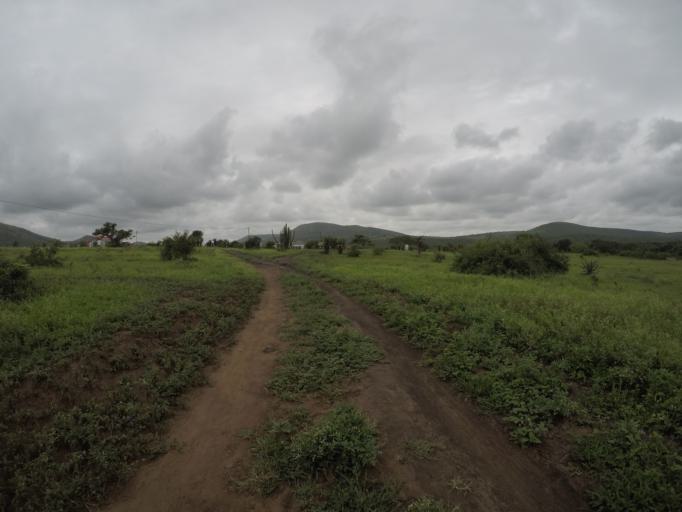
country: ZA
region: KwaZulu-Natal
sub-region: uThungulu District Municipality
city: Empangeni
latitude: -28.6075
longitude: 31.8710
